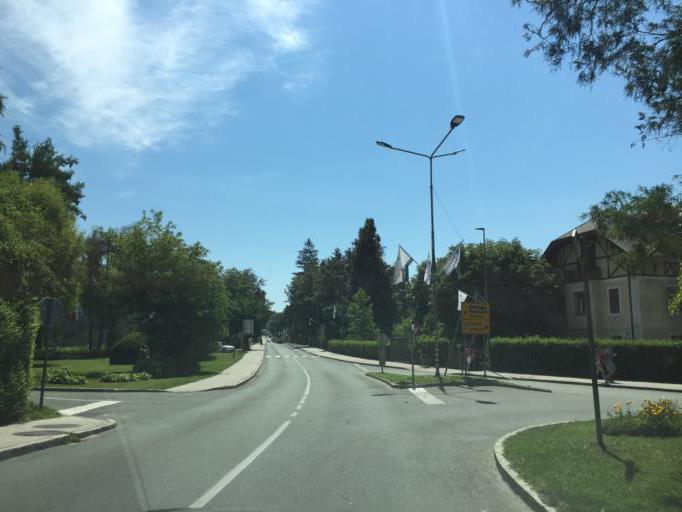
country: SI
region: Bled
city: Bled
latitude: 46.3714
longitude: 14.1078
